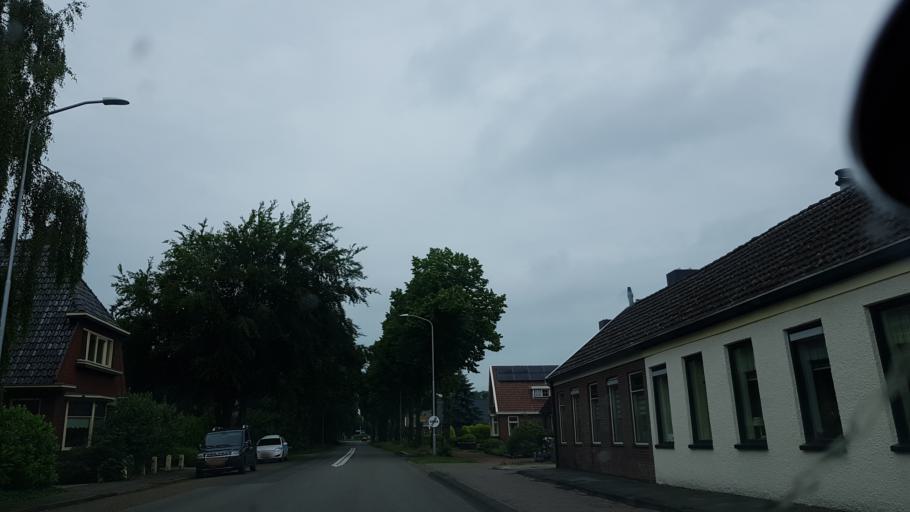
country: NL
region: Groningen
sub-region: Gemeente Hoogezand-Sappemeer
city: Hoogezand
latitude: 53.1491
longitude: 6.7236
